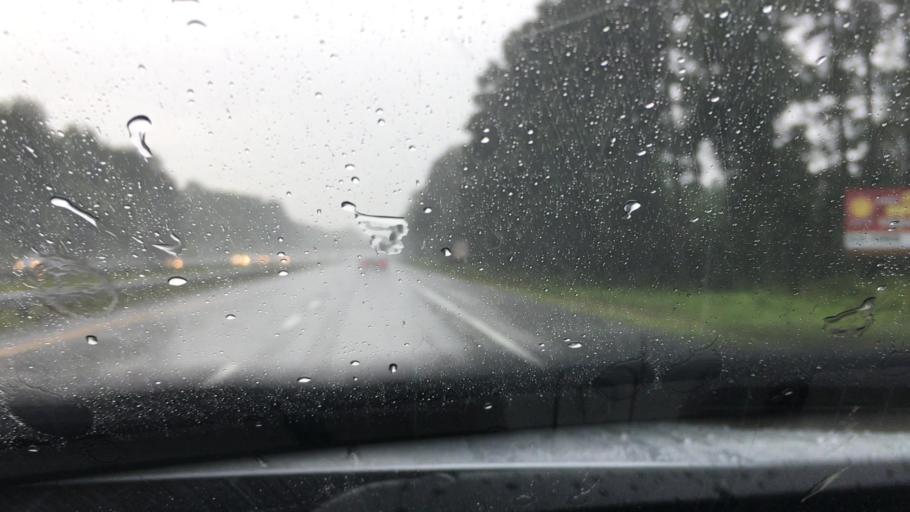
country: US
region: North Carolina
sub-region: Halifax County
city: Halifax
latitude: 36.3571
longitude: -77.6778
